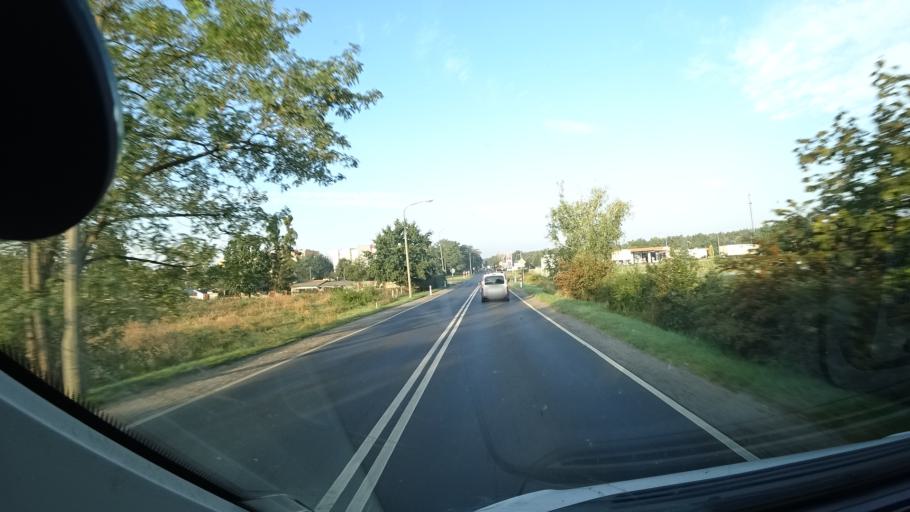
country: PL
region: Opole Voivodeship
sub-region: Powiat kedzierzynsko-kozielski
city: Kedzierzyn-Kozle
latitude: 50.3529
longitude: 18.2396
